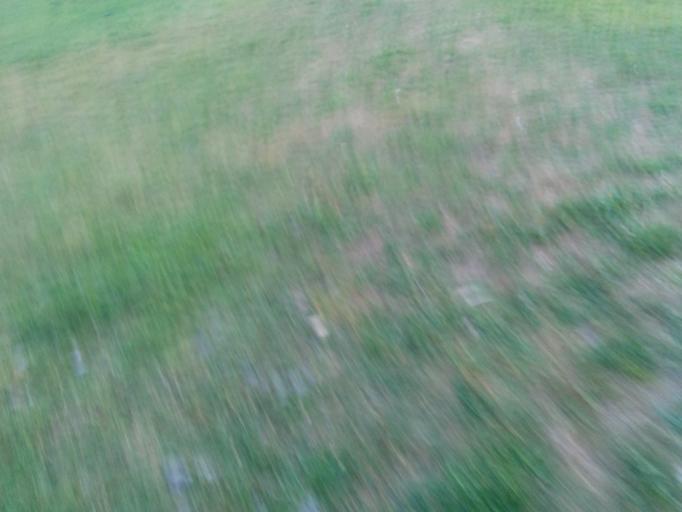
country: DE
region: North Rhine-Westphalia
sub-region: Regierungsbezirk Dusseldorf
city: Hochfeld
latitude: 51.4430
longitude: 6.7156
